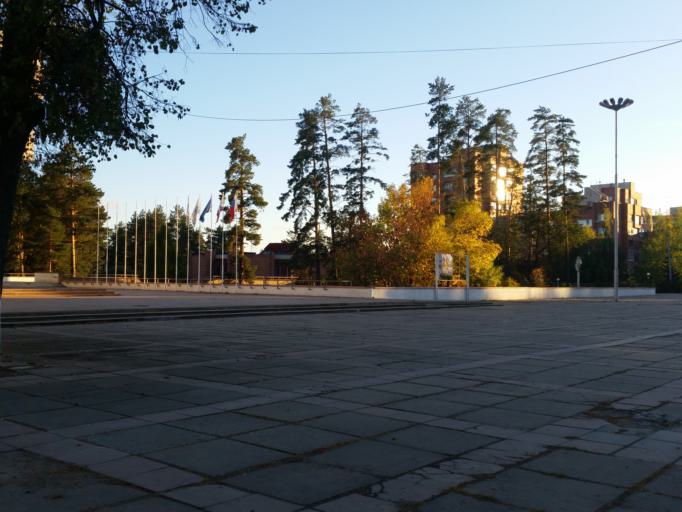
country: RU
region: Ulyanovsk
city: Dimitrovgrad
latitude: 54.2285
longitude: 49.5599
